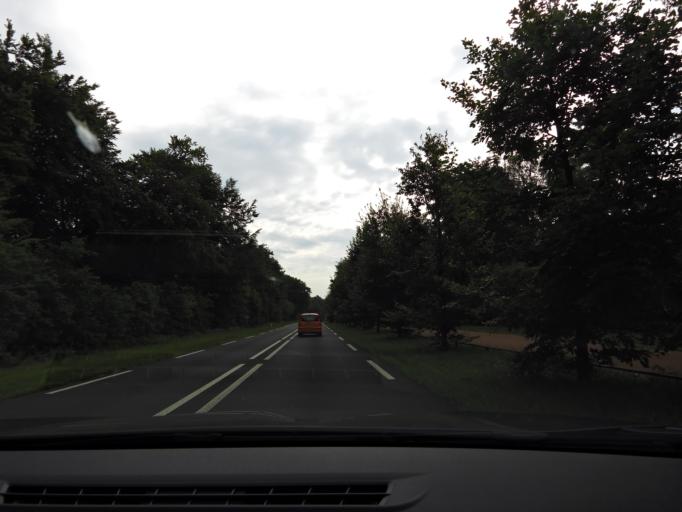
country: NL
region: Gelderland
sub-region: Gemeente Renkum
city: Doorwerth
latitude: 51.9853
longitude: 5.7857
